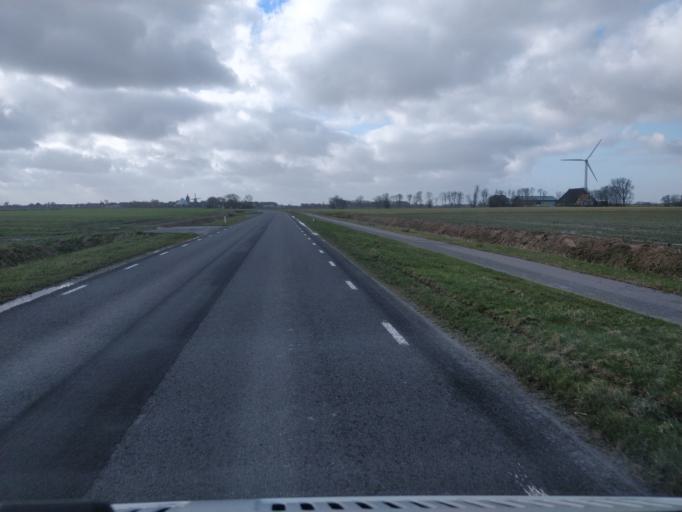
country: NL
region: Friesland
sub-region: Gemeente Franekeradeel
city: Sexbierum
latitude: 53.2295
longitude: 5.5003
